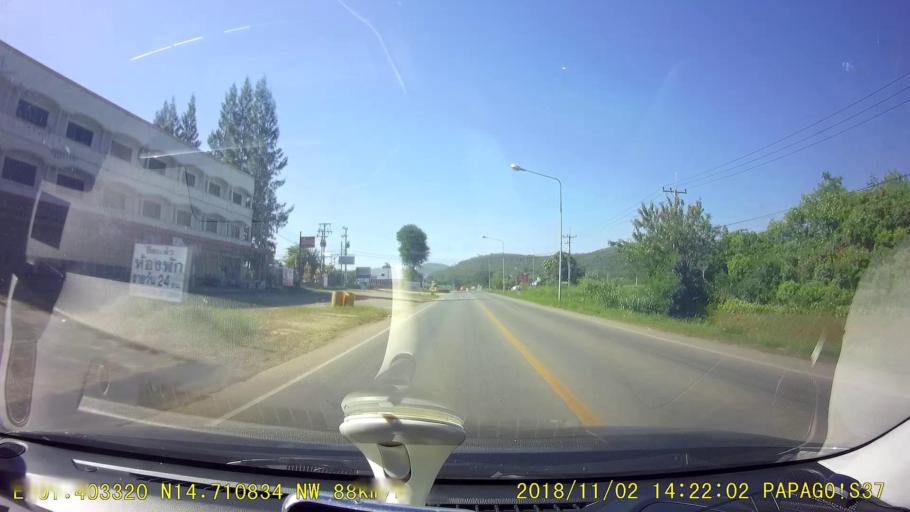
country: TH
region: Nakhon Ratchasima
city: Pak Chong
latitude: 14.7112
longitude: 101.4030
